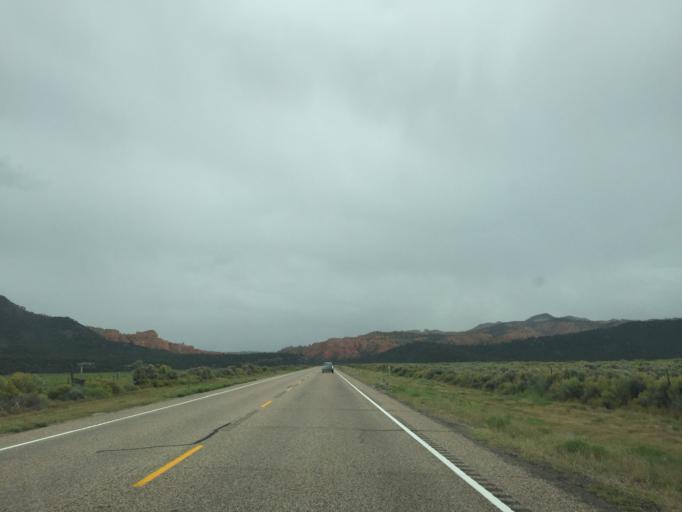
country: US
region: Utah
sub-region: Garfield County
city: Panguitch
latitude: 37.7473
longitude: -112.3534
